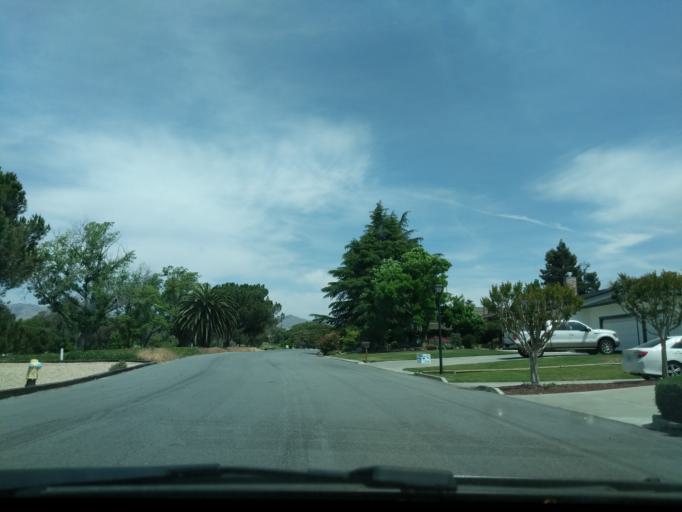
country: US
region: California
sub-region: San Benito County
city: Ridgemark
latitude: 36.8109
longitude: -121.3583
